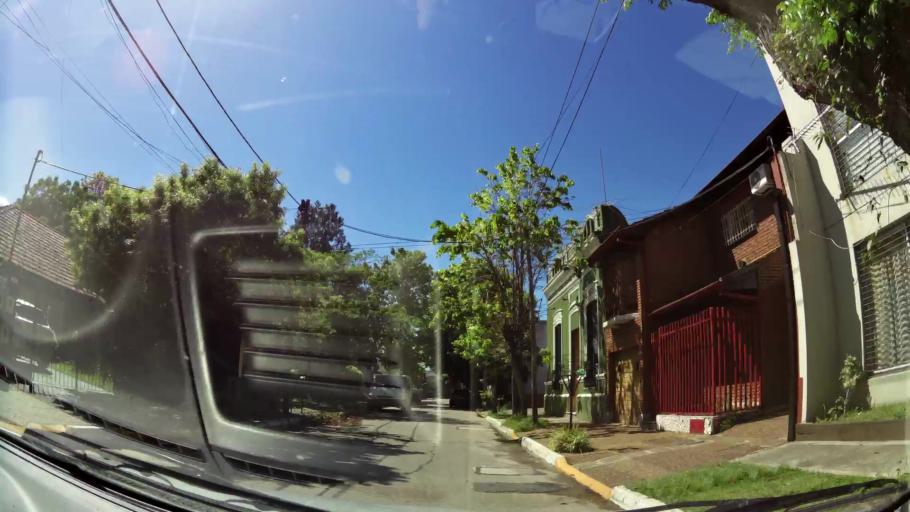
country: AR
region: Buenos Aires
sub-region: Partido de Quilmes
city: Quilmes
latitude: -34.7041
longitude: -58.2840
